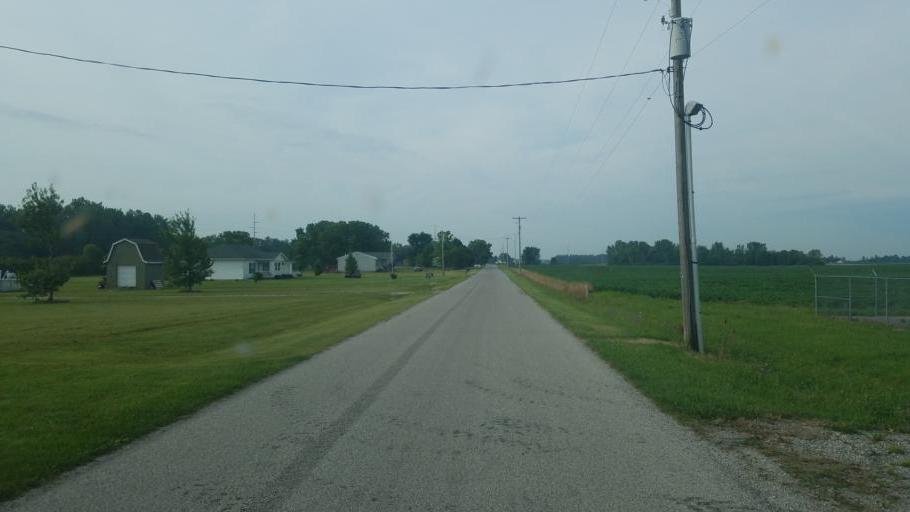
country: US
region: Ohio
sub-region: Morrow County
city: Cardington
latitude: 40.5405
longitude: -82.8767
